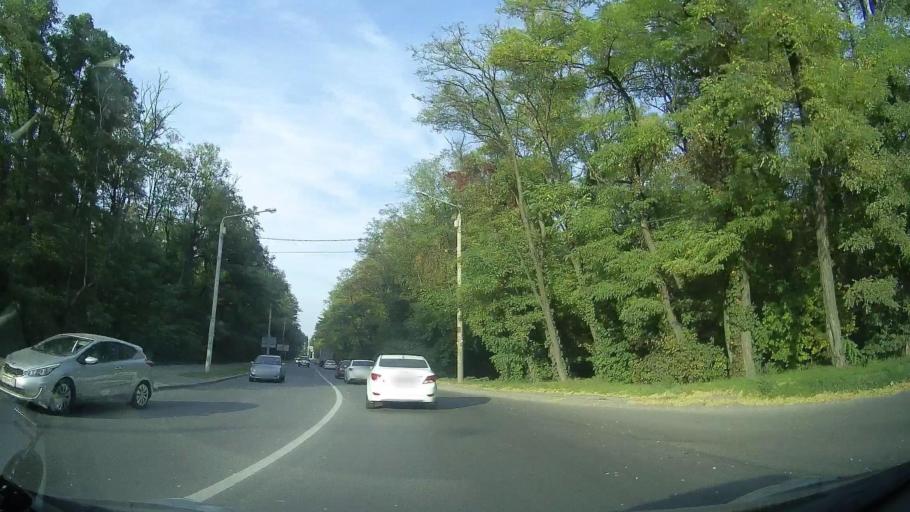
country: RU
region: Rostov
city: Imeni Chkalova
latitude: 47.2746
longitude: 39.7950
